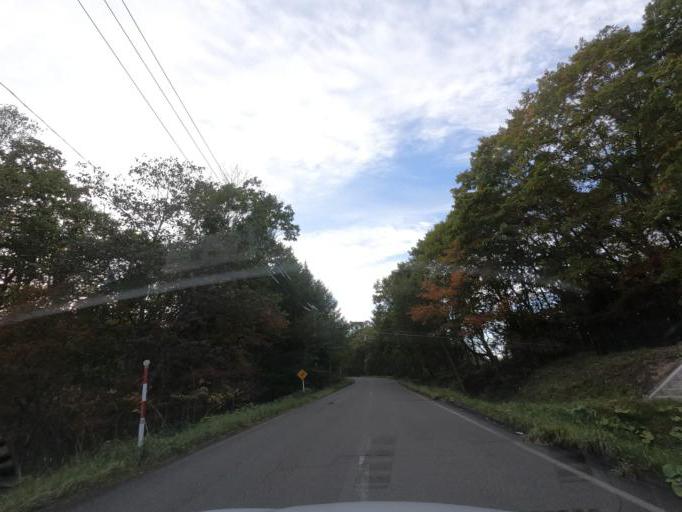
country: JP
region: Hokkaido
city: Obihiro
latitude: 42.5371
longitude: 143.4328
